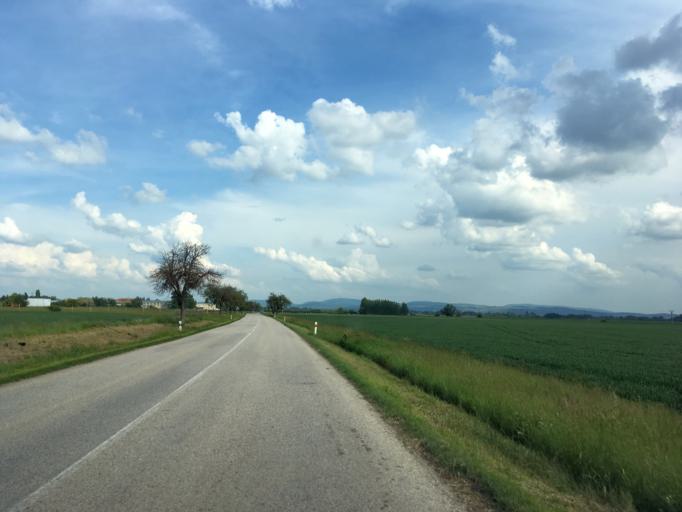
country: HU
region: Komarom-Esztergom
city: Almasfuzito
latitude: 47.7911
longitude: 18.2564
